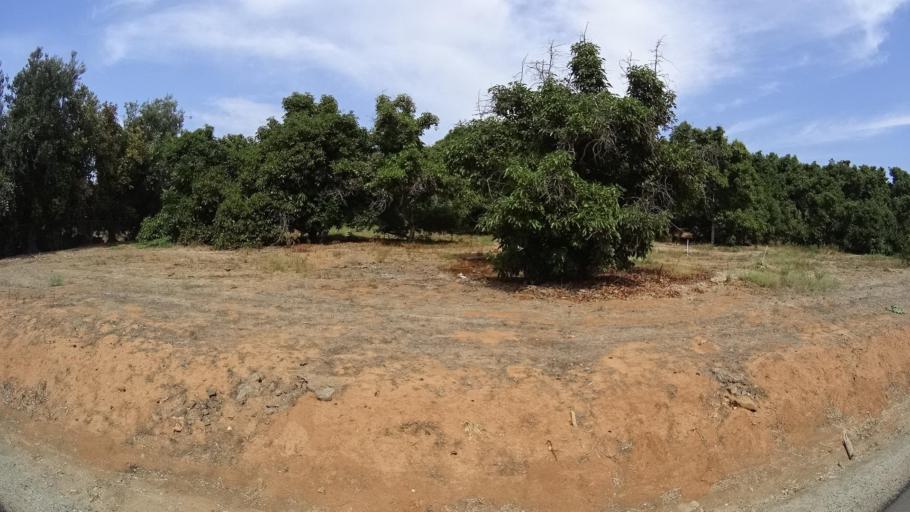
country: US
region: California
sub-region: San Diego County
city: Escondido
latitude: 33.1127
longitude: -117.0379
